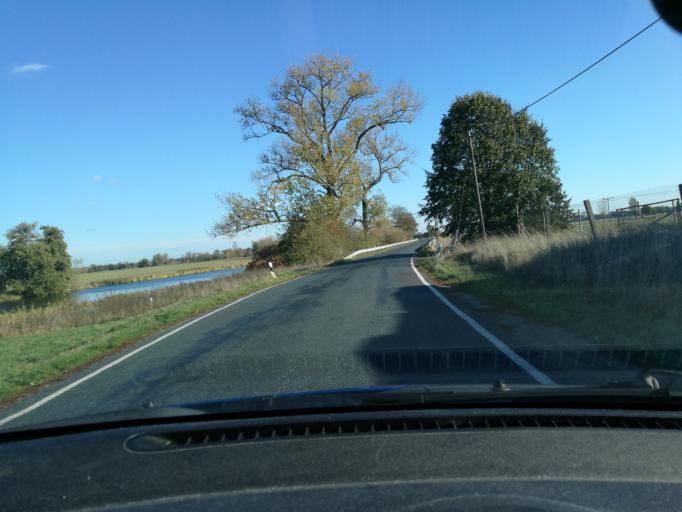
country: DE
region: Lower Saxony
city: Gorleben
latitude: 53.1086
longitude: 11.3863
